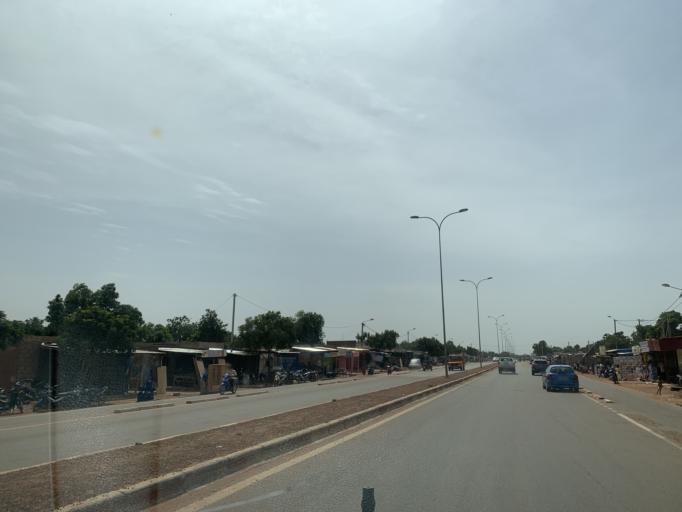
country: BF
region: Centre
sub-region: Kadiogo Province
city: Ouagadougou
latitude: 12.3394
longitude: -1.5177
